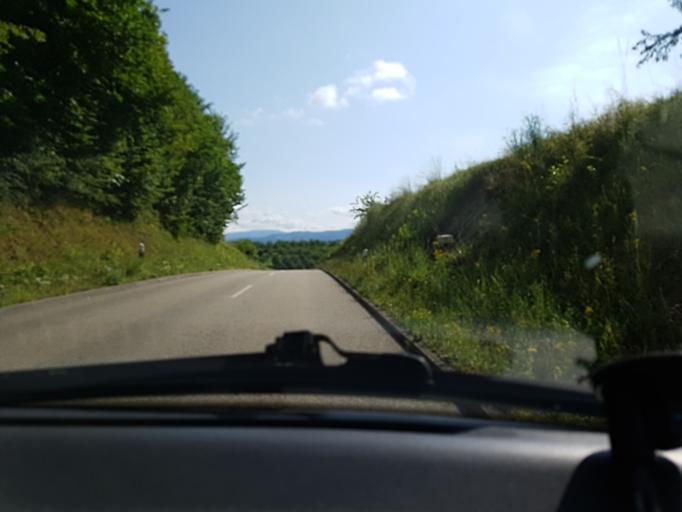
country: DE
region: Baden-Wuerttemberg
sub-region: Freiburg Region
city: Durbach
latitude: 48.5097
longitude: 7.9977
